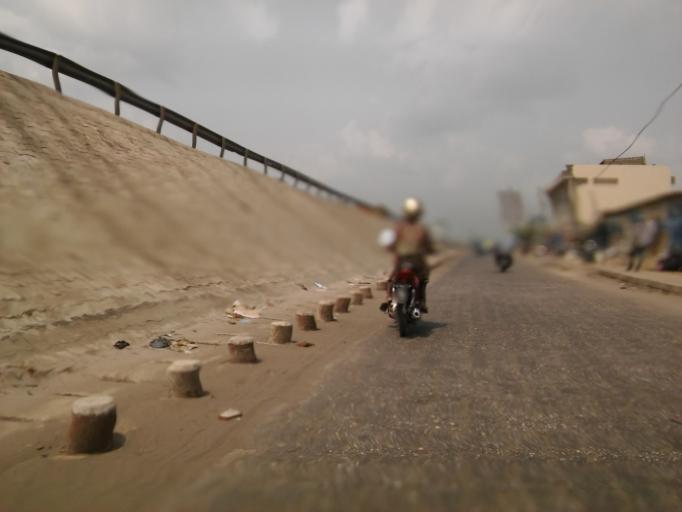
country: BJ
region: Atlantique
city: Abomey-Calavi
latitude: 6.3903
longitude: 2.3532
